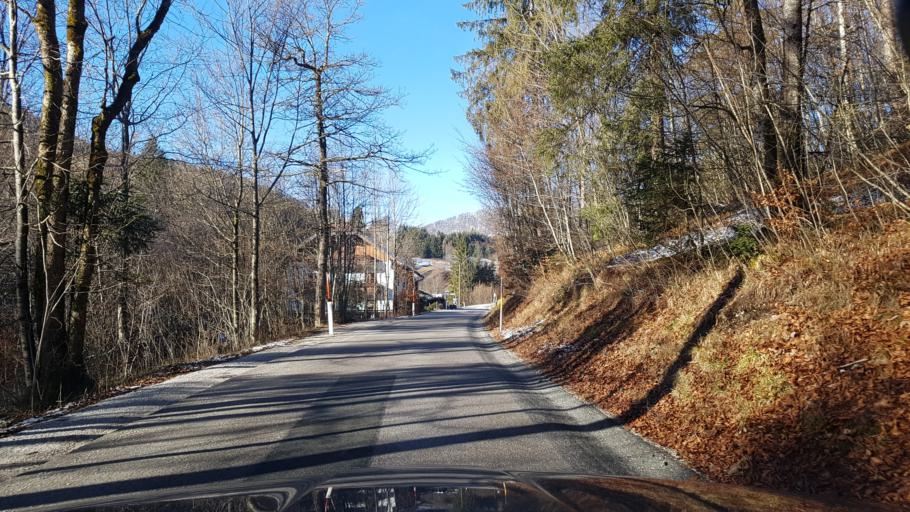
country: AT
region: Salzburg
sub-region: Politischer Bezirk Salzburg-Umgebung
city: Ebenau
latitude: 47.7679
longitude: 13.1750
